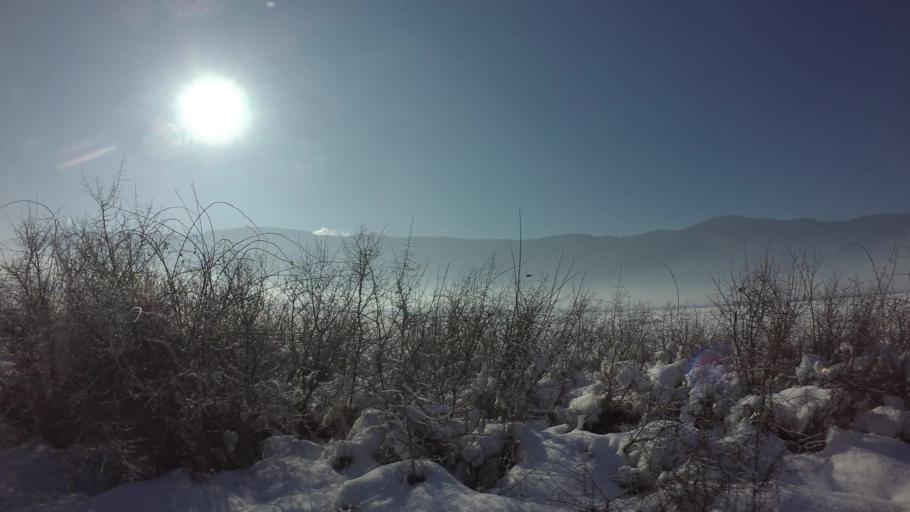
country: BA
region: Federation of Bosnia and Herzegovina
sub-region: Kanton Sarajevo
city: Sarajevo
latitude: 43.7992
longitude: 18.3345
